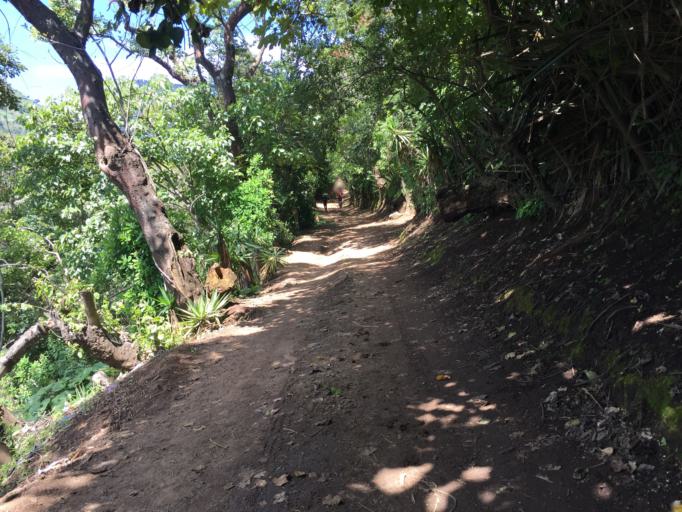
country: GT
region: Sacatepequez
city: Magdalena Milpas Altas
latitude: 14.5107
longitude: -90.6582
